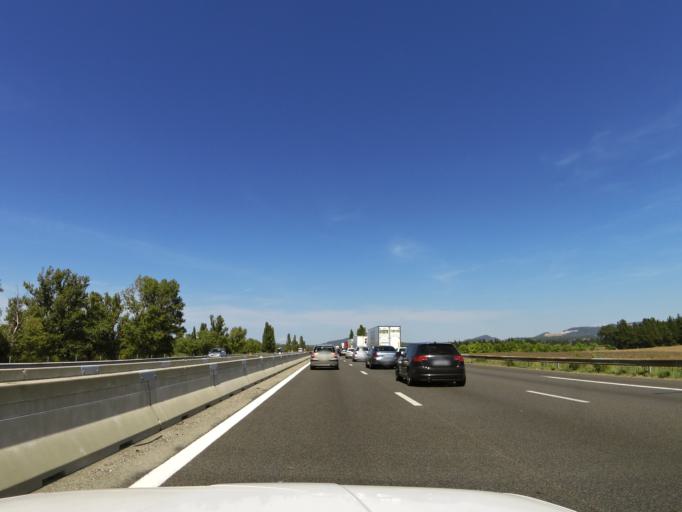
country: FR
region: Rhone-Alpes
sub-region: Departement de la Drome
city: La Garde-Adhemar
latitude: 44.3860
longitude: 4.7311
